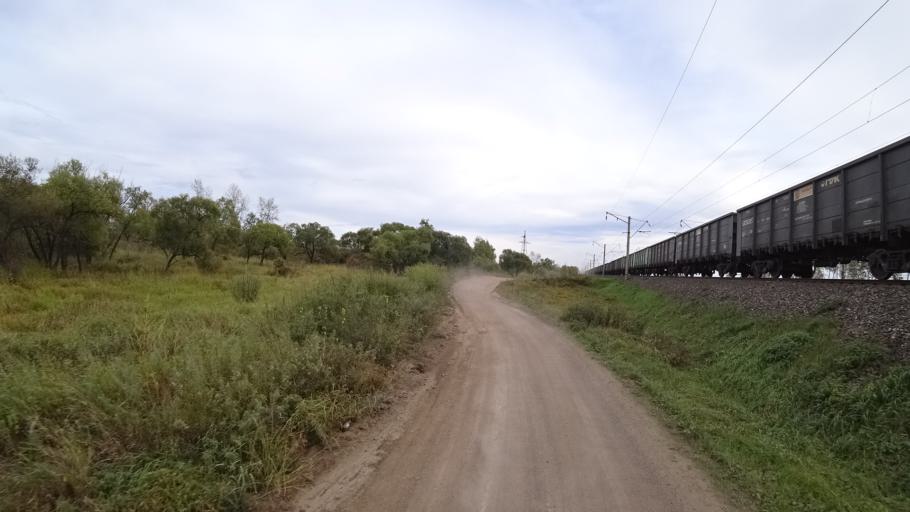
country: RU
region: Amur
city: Arkhara
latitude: 49.3662
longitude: 130.1445
